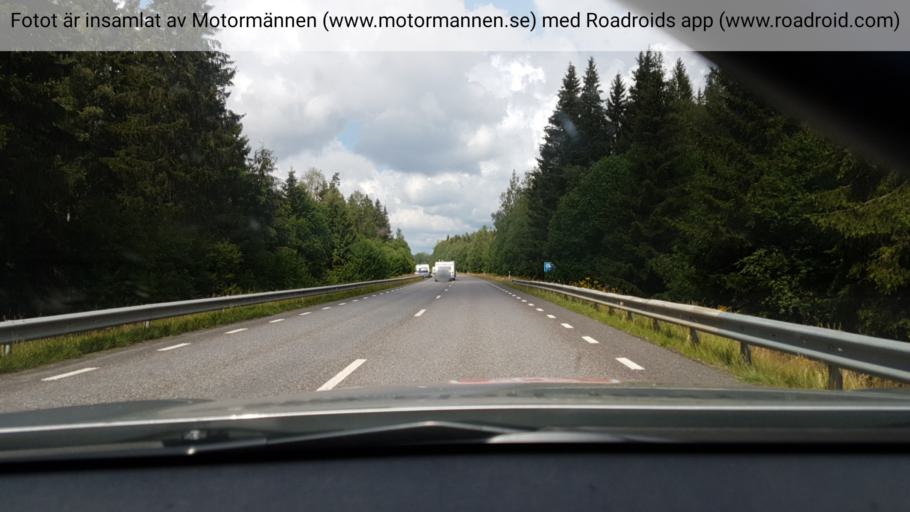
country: SE
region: Vaestra Goetaland
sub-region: Tranemo Kommun
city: Tranemo
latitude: 57.4832
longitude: 13.3701
